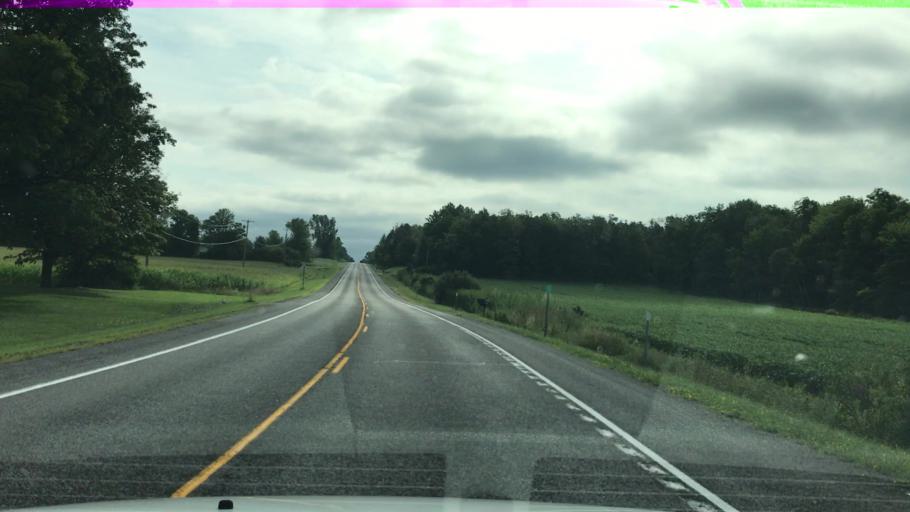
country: US
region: New York
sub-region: Erie County
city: Alden
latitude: 42.8349
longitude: -78.4473
